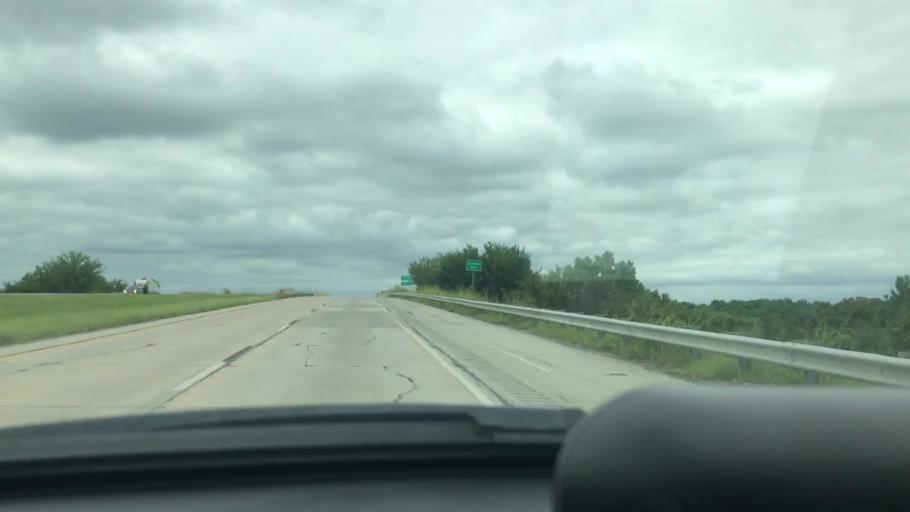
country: US
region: Oklahoma
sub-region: Wagoner County
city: Wagoner
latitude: 35.8834
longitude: -95.4026
